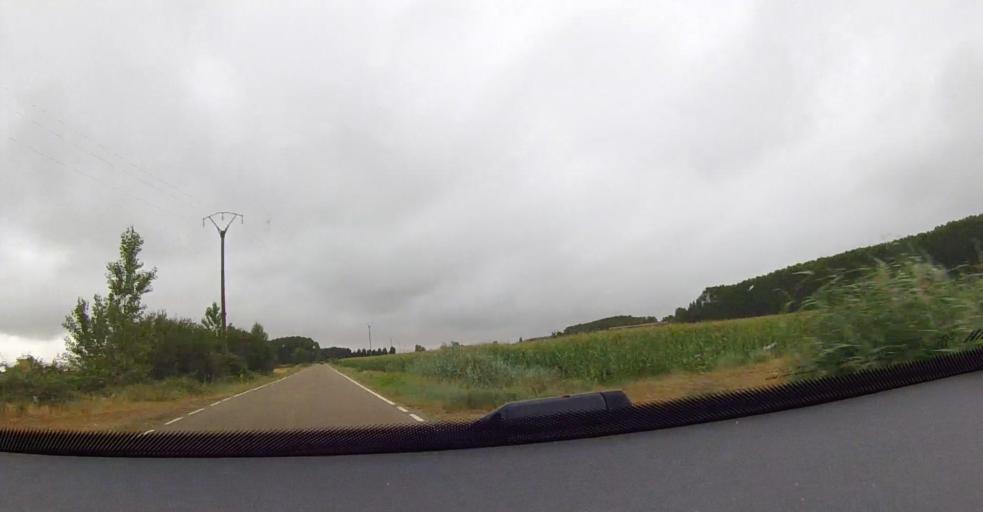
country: ES
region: Castille and Leon
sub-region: Provincia de Palencia
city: Pedrosa de la Vega
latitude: 42.4808
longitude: -4.7288
